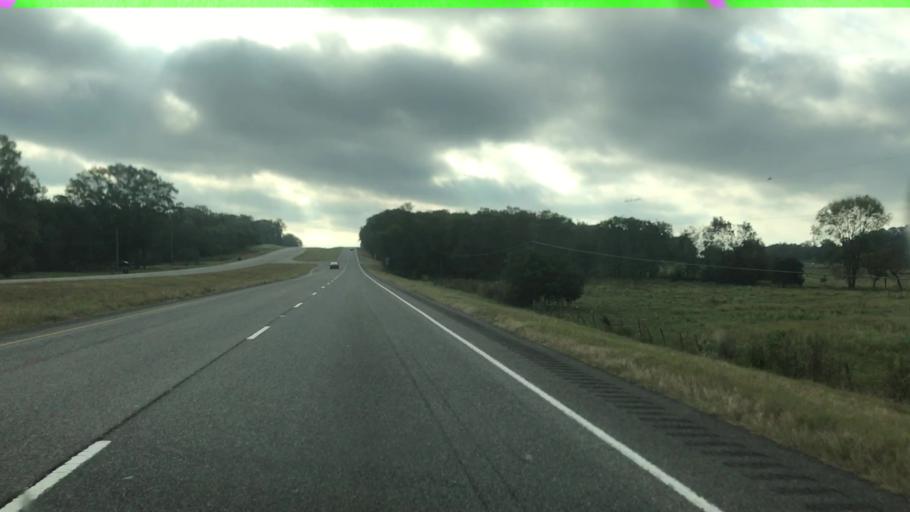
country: US
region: Alabama
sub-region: Morgan County
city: Danville
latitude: 34.4008
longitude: -87.1326
